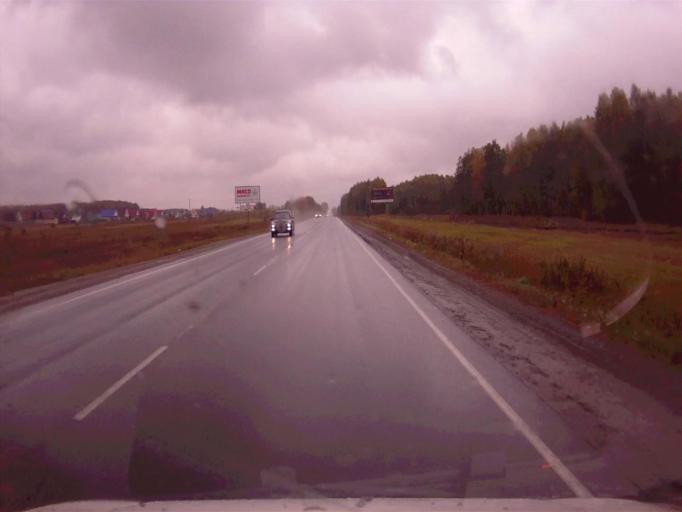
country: RU
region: Chelyabinsk
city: Argayash
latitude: 55.4200
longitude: 61.0182
